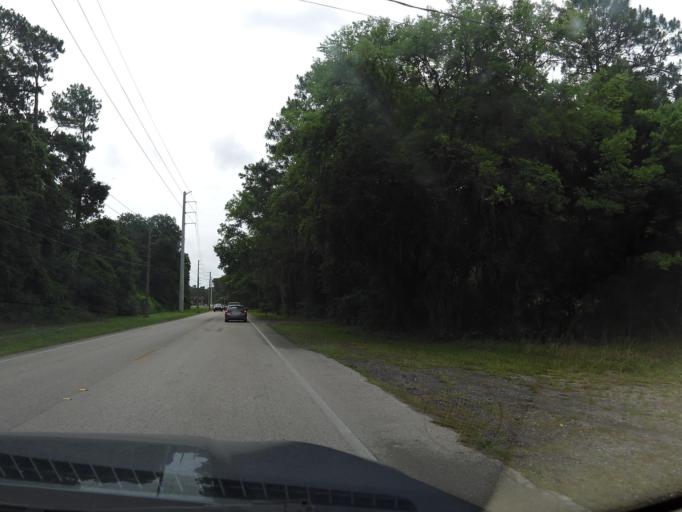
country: US
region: Florida
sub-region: Saint Johns County
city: Saint Augustine
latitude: 29.9109
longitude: -81.3643
